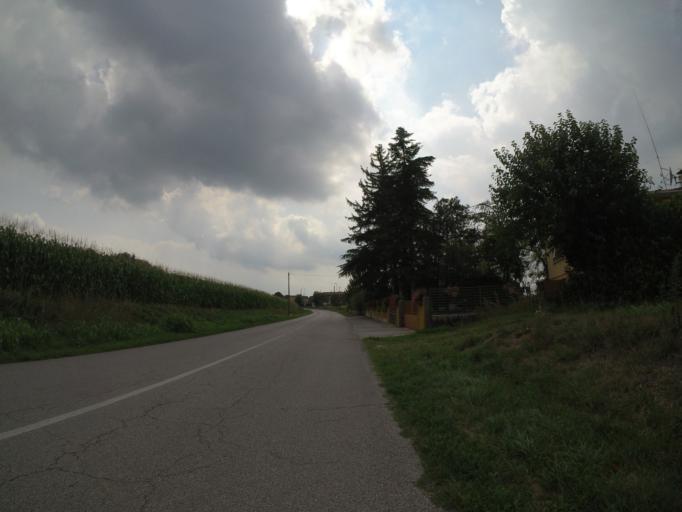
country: IT
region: Friuli Venezia Giulia
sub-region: Provincia di Udine
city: Sedegliano
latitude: 46.0060
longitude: 13.0030
